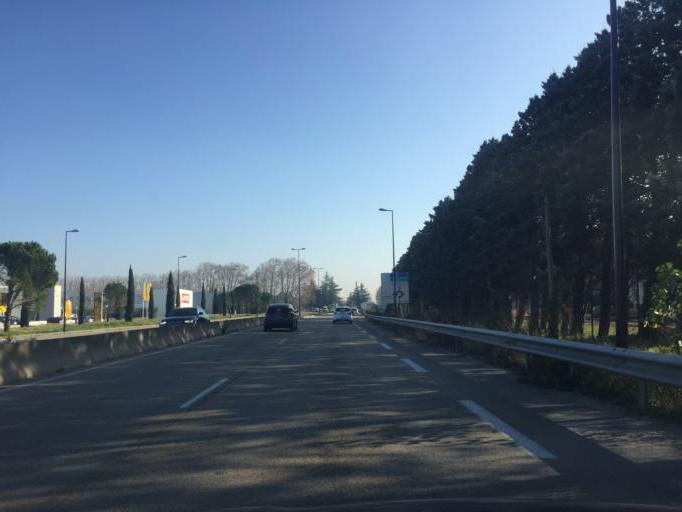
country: FR
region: Provence-Alpes-Cote d'Azur
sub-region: Departement du Vaucluse
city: Montfavet
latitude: 43.9173
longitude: 4.8710
